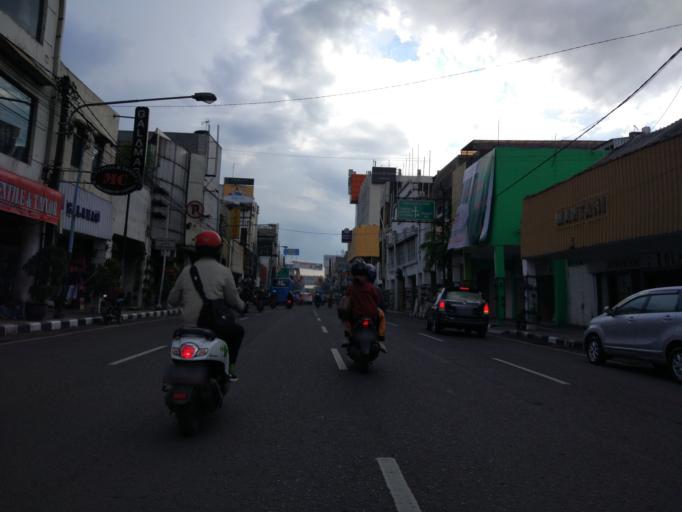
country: ID
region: West Java
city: Bandung
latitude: -6.9210
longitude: 107.6060
